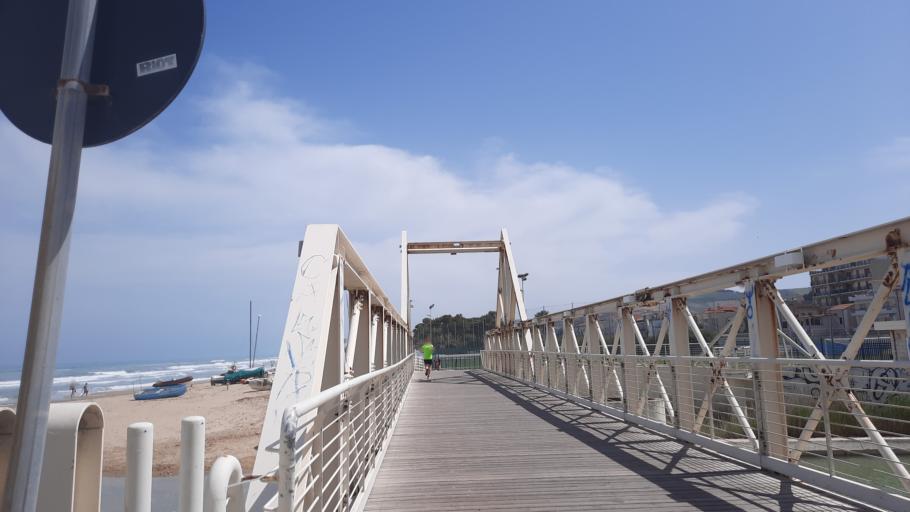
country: IT
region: Abruzzo
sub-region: Provincia di Teramo
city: Pineto
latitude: 42.6124
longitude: 14.0665
